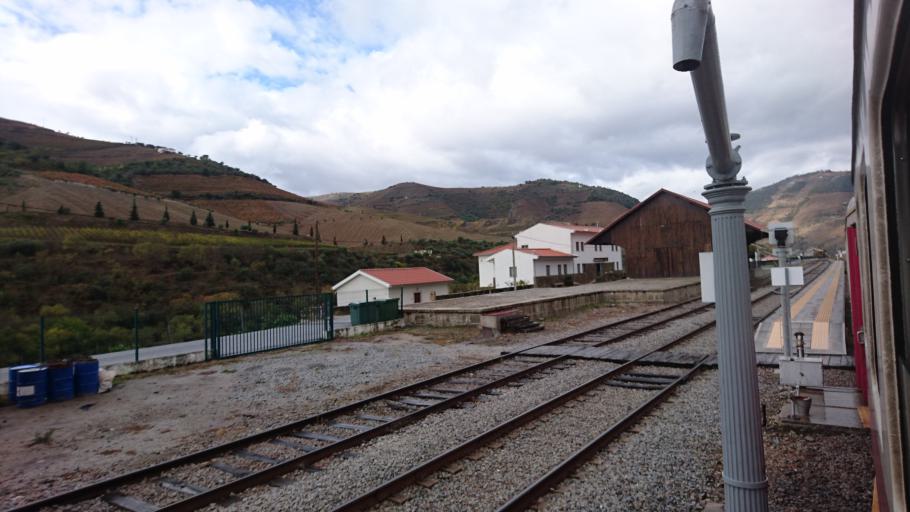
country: PT
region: Viseu
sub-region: Sao Joao da Pesqueira
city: Sao Joao da Pesqueira
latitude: 41.2070
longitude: -7.4187
